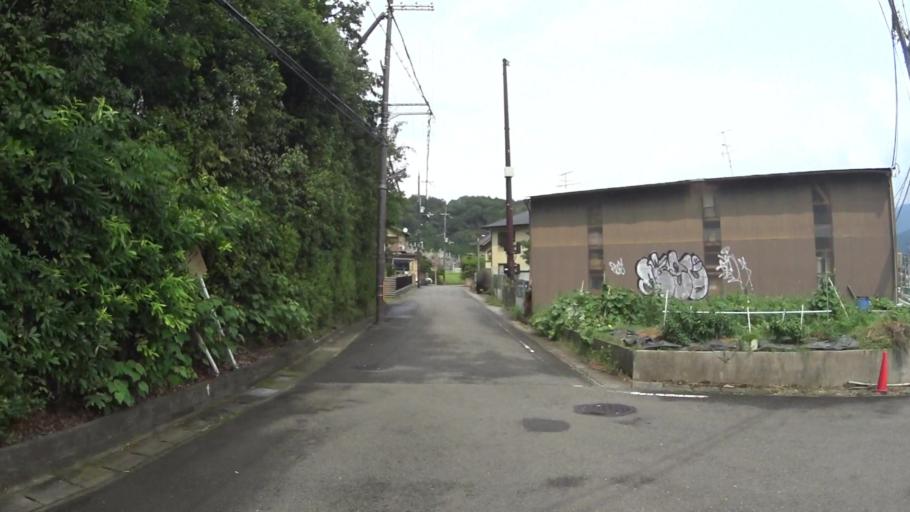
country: JP
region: Kyoto
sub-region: Kyoto-shi
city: Kamigyo-ku
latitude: 35.0719
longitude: 135.7811
